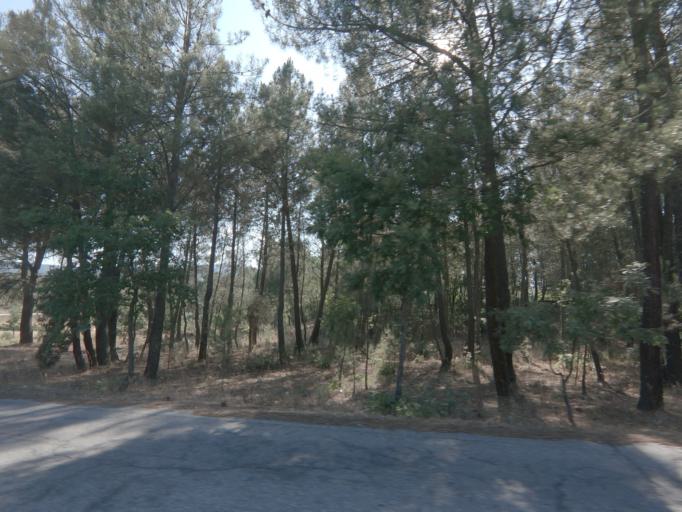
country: PT
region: Viseu
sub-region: Moimenta da Beira
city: Moimenta da Beira
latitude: 40.9753
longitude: -7.5773
